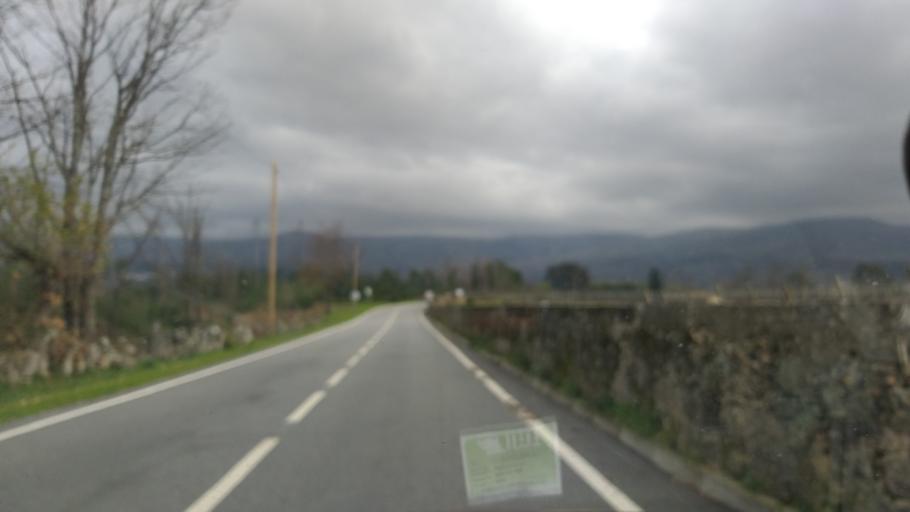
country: PT
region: Guarda
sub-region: Seia
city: Seia
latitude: 40.4785
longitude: -7.6506
